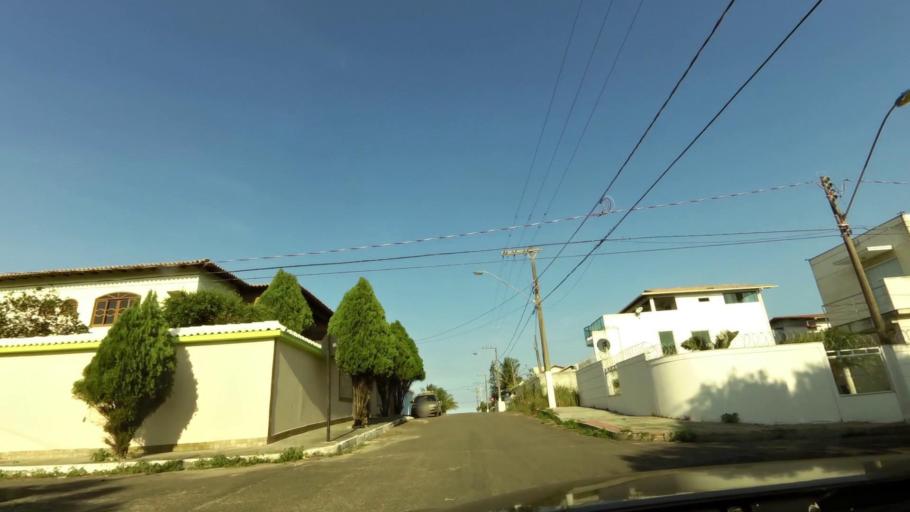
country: BR
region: Espirito Santo
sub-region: Vila Velha
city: Vila Velha
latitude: -20.4751
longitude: -40.3481
